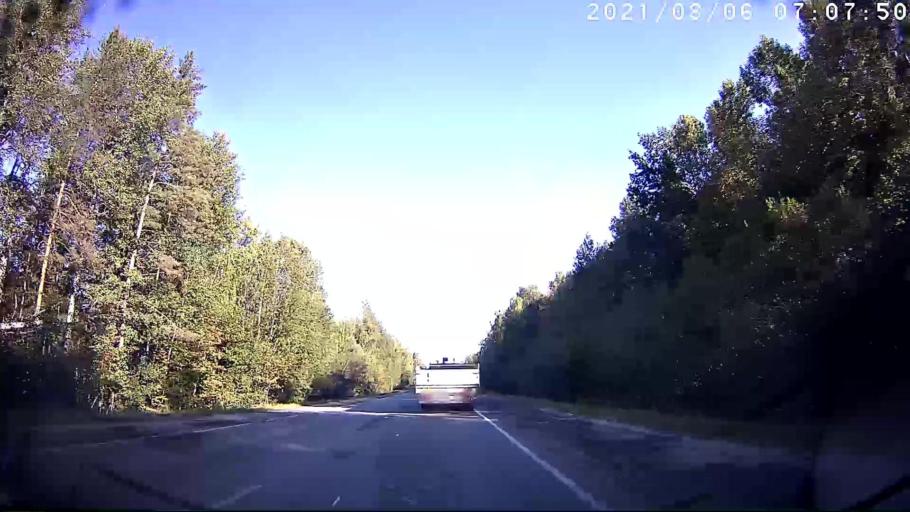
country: RU
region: Mariy-El
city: Yoshkar-Ola
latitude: 56.5658
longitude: 47.9762
